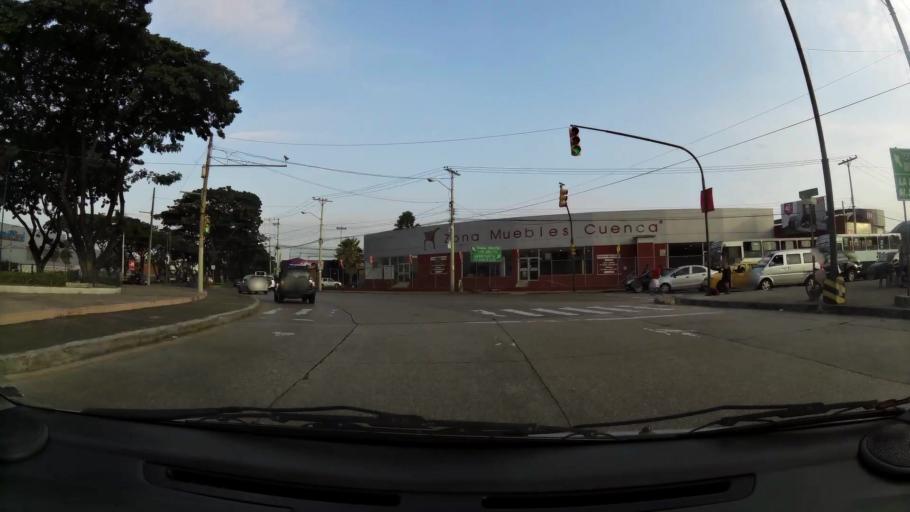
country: EC
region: Guayas
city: Eloy Alfaro
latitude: -2.1418
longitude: -79.8893
